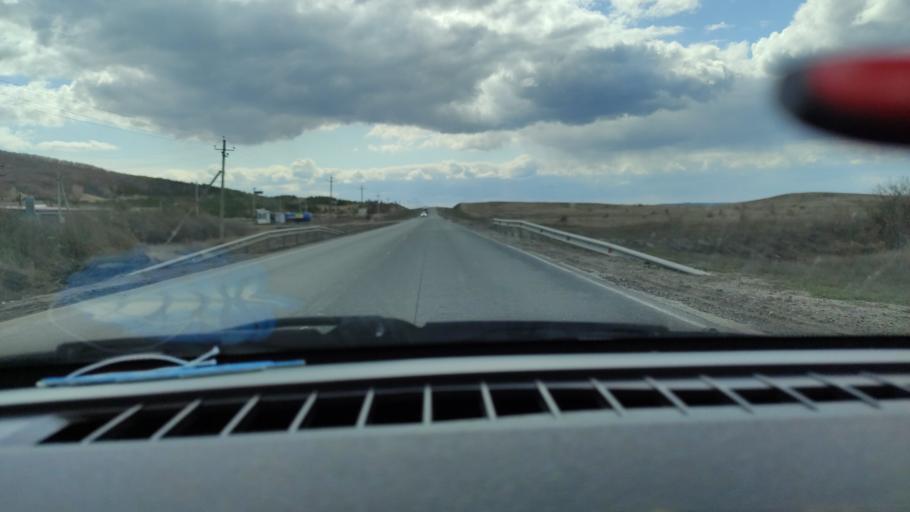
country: RU
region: Saratov
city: Alekseyevka
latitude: 52.3028
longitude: 47.9267
